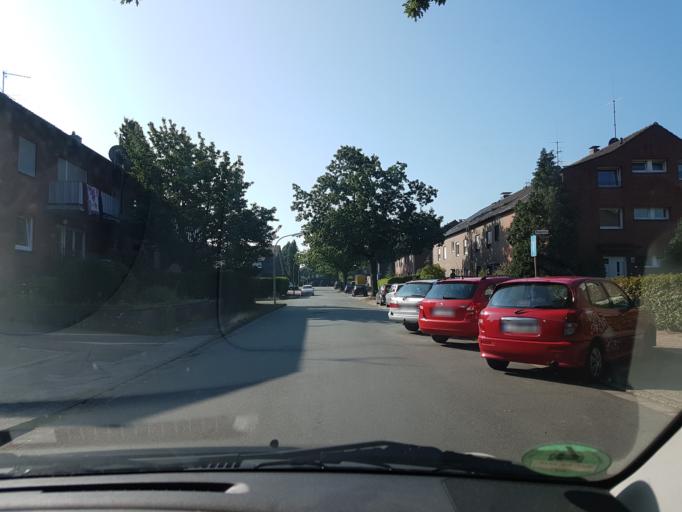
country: DE
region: North Rhine-Westphalia
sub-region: Regierungsbezirk Munster
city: Heiden
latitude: 51.7556
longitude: 6.9553
